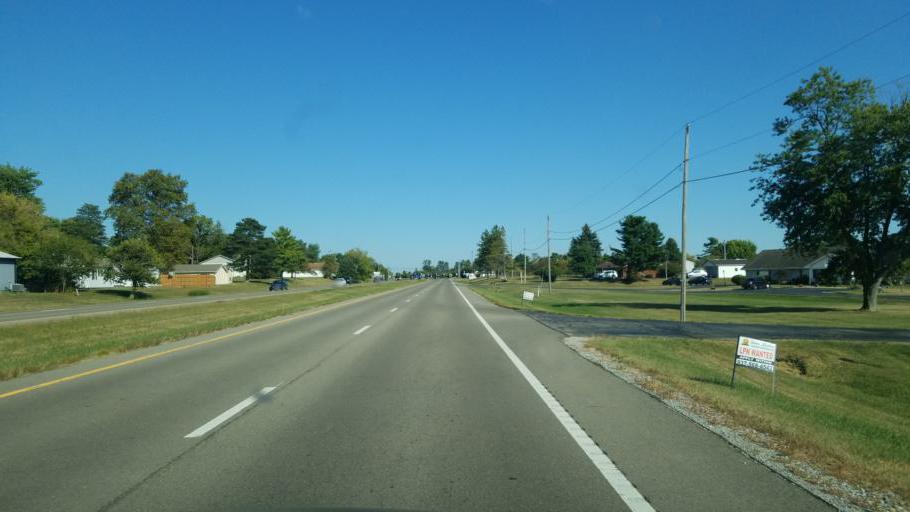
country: US
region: Ohio
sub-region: Clark County
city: Lisbon
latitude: 39.9270
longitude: -83.6180
